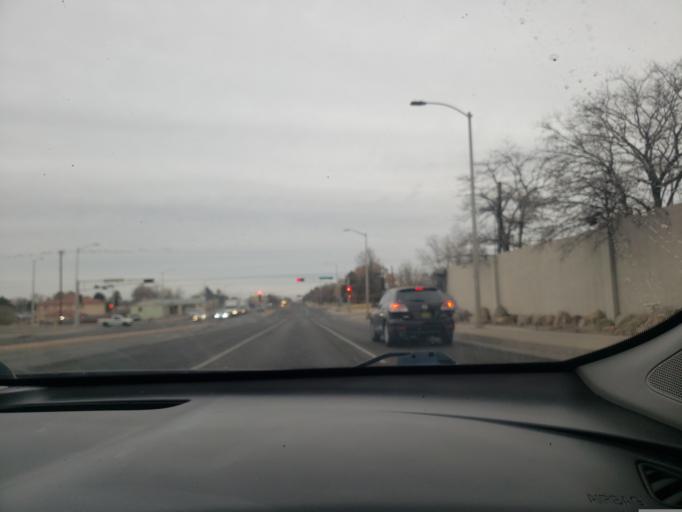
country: US
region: New Mexico
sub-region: Bernalillo County
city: Albuquerque
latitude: 35.0939
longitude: -106.5862
